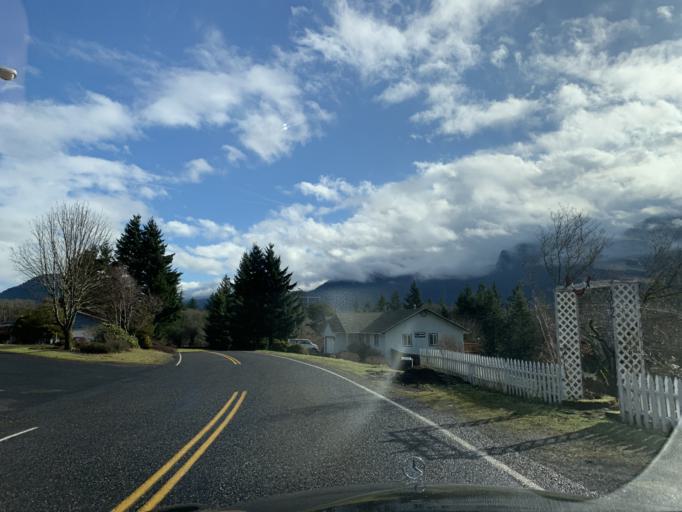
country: US
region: Washington
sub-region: Skamania County
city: Carson
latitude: 45.7194
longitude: -121.8169
